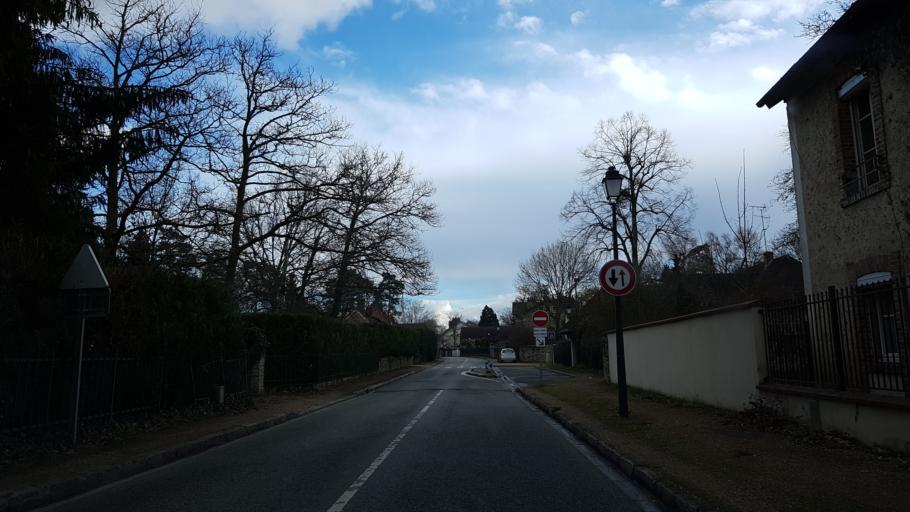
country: FR
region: Ile-de-France
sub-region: Departement des Yvelines
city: Sonchamp
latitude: 48.6191
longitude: 1.9047
